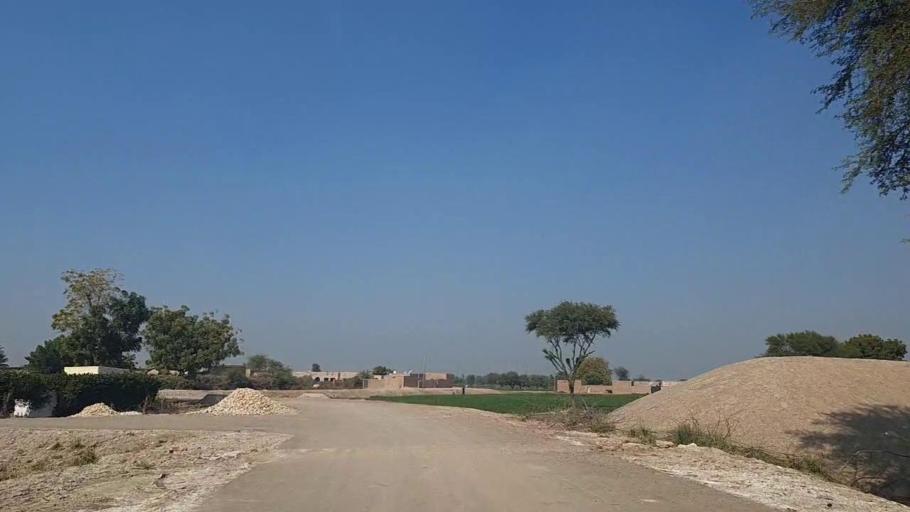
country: PK
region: Sindh
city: Nawabshah
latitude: 26.2285
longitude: 68.3432
